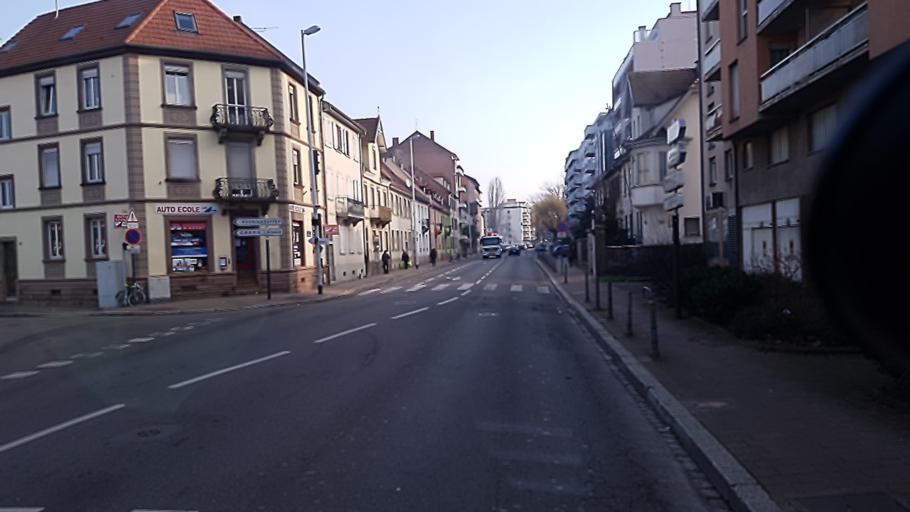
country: FR
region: Alsace
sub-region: Departement du Bas-Rhin
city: Eckbolsheim
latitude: 48.5721
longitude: 7.7141
